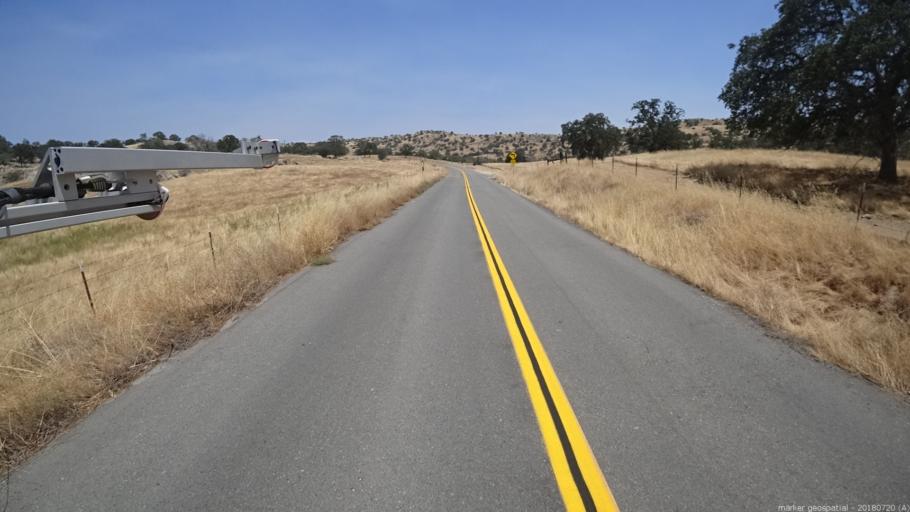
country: US
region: California
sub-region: Madera County
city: Yosemite Lakes
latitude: 37.1226
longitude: -119.8596
